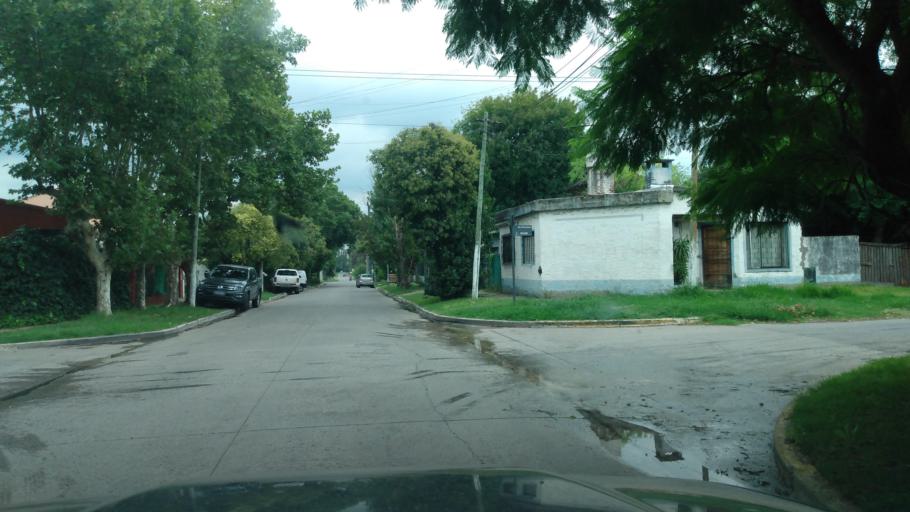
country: AR
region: Buenos Aires
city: Hurlingham
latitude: -34.5722
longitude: -58.6970
